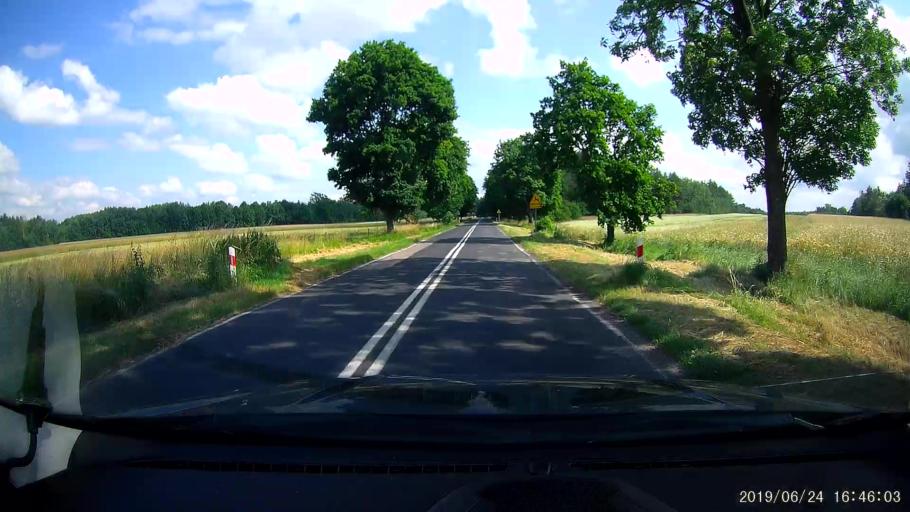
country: PL
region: Lublin Voivodeship
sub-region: Powiat tomaszowski
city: Laszczow
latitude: 50.5295
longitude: 23.6728
